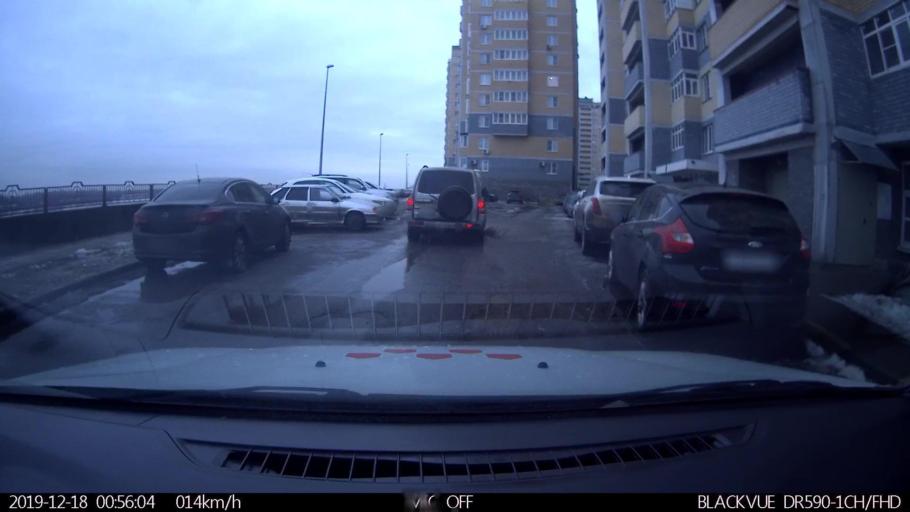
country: RU
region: Nizjnij Novgorod
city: Nizhniy Novgorod
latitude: 56.3496
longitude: 43.9295
